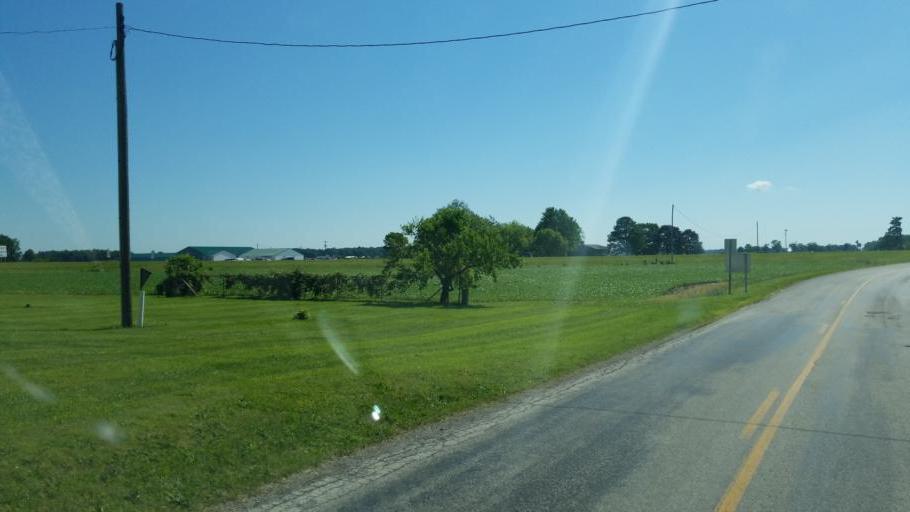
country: US
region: Ohio
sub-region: Marion County
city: Marion
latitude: 40.6520
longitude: -83.1076
